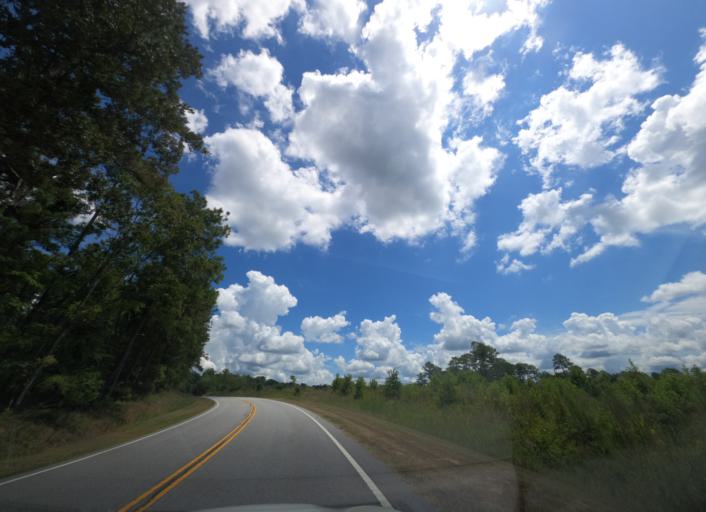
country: US
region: South Carolina
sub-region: McCormick County
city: McCormick
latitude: 33.8858
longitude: -82.4073
